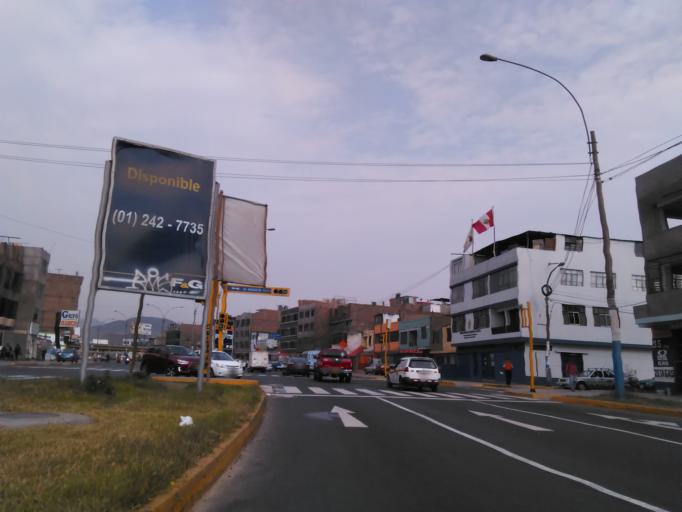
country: PE
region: Lima
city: Lima
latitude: -12.0300
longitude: -77.0607
